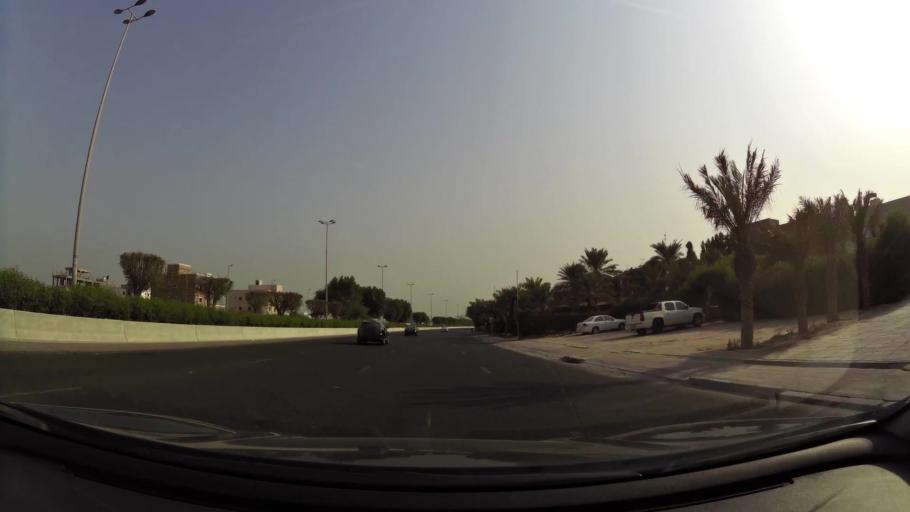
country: KW
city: Al Funaytis
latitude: 29.2208
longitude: 48.0867
